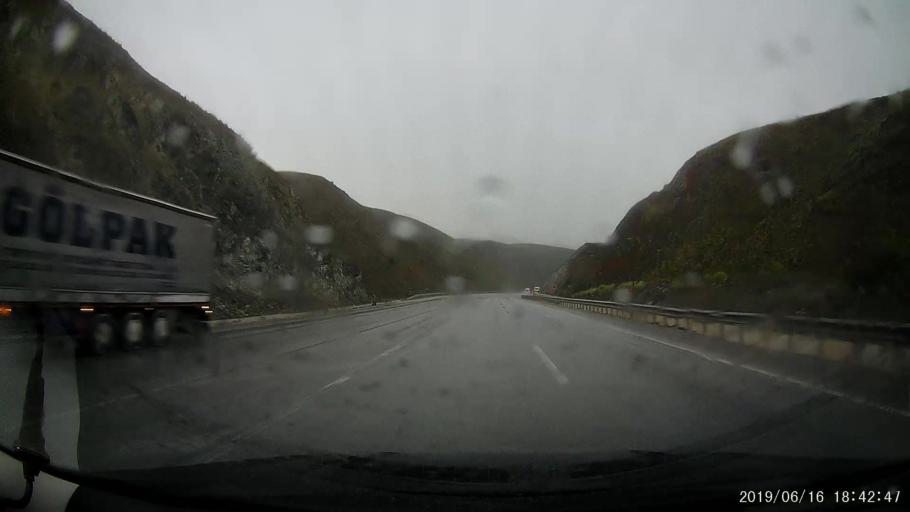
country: TR
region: Erzincan
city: Doganbeyli
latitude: 39.8680
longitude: 39.1021
